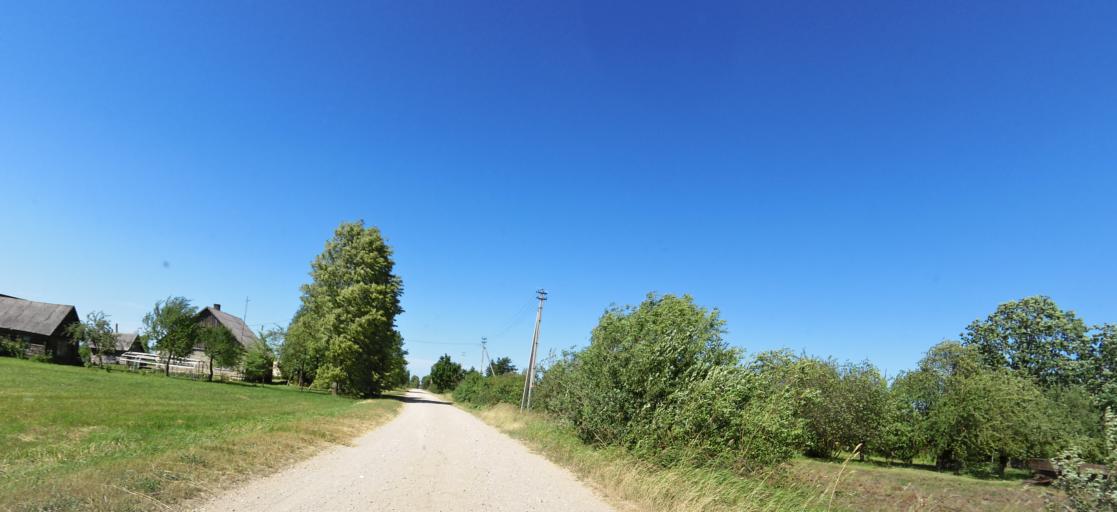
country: LT
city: Vabalninkas
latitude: 55.9275
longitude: 24.6516
